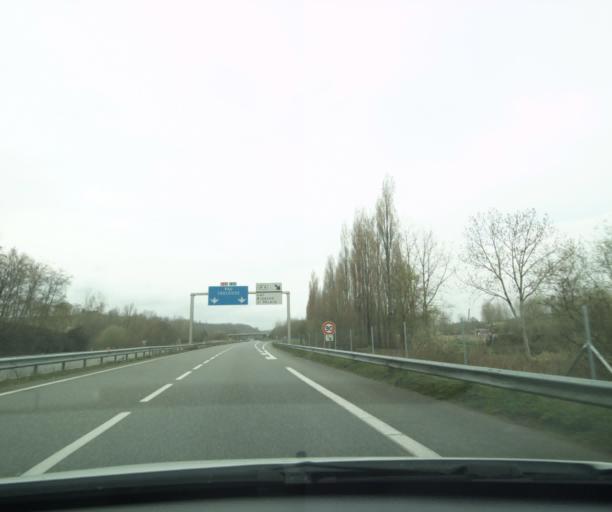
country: FR
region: Aquitaine
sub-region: Departement des Pyrenees-Atlantiques
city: Urt
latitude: 43.4639
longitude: -1.2886
